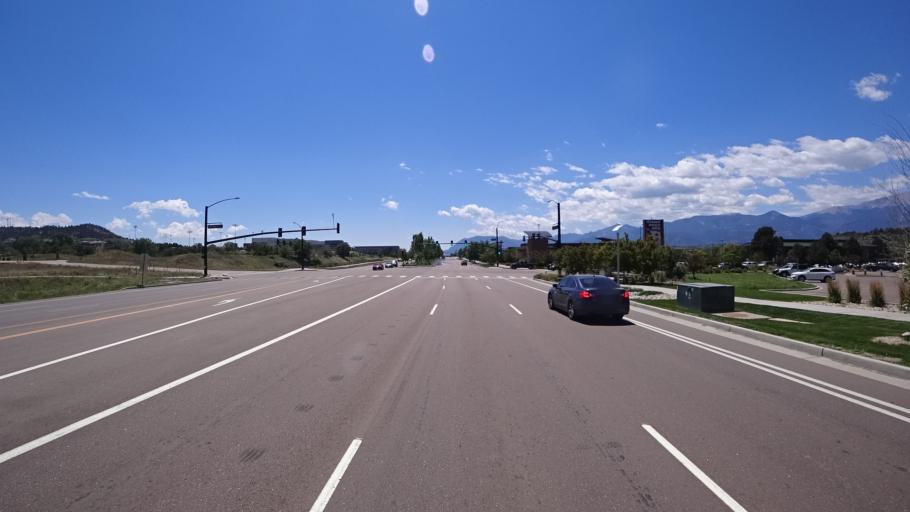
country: US
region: Colorado
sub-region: El Paso County
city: Colorado Springs
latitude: 38.9085
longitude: -104.8172
